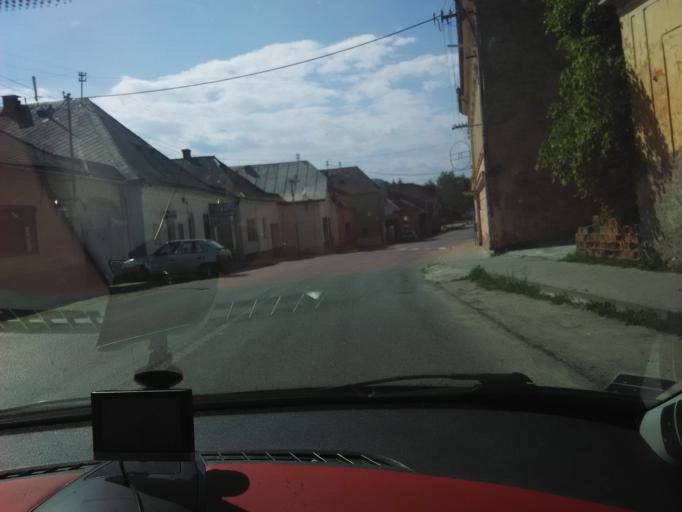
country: SK
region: Banskobystricky
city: Revuca
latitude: 48.6283
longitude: 20.2379
